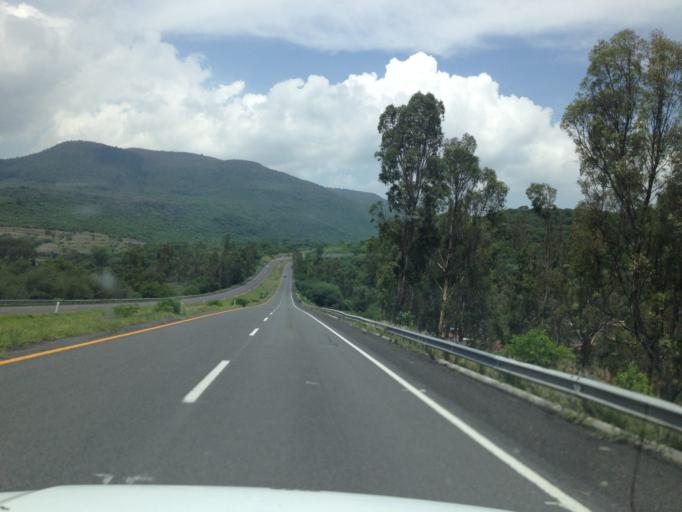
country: MX
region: Mexico
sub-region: Chapultepec
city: Chucandiro
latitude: 19.8966
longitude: -101.3056
